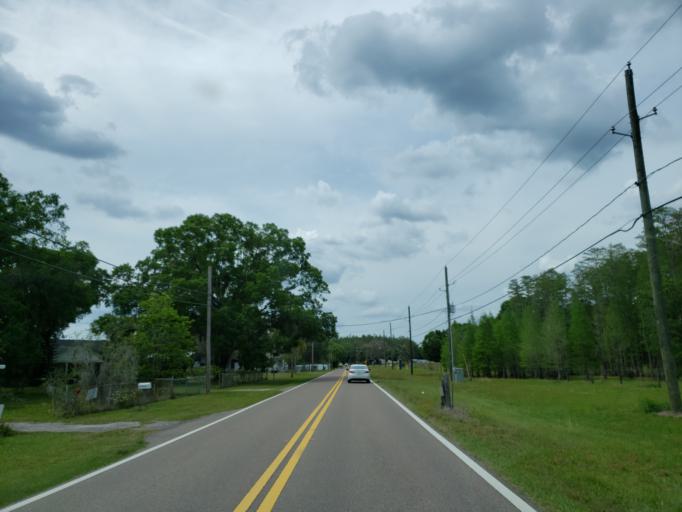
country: US
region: Florida
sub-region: Hillsborough County
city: Keystone
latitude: 28.1269
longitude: -82.6147
